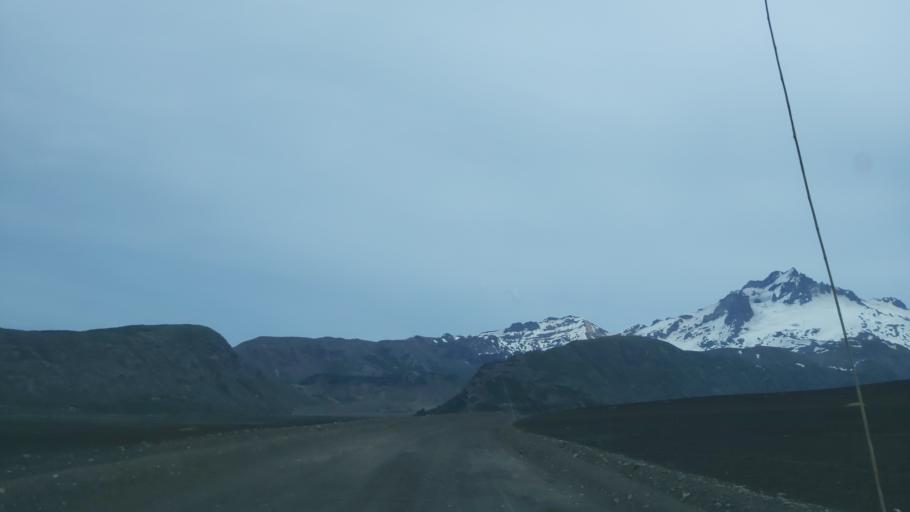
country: AR
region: Neuquen
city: Andacollo
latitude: -37.4568
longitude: -71.2968
